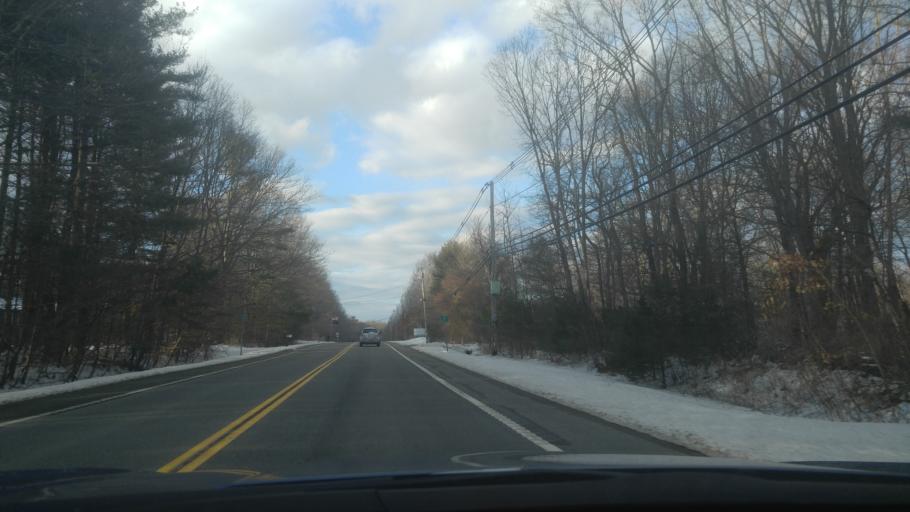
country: US
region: Rhode Island
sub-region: Kent County
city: Coventry
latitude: 41.7099
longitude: -71.6988
